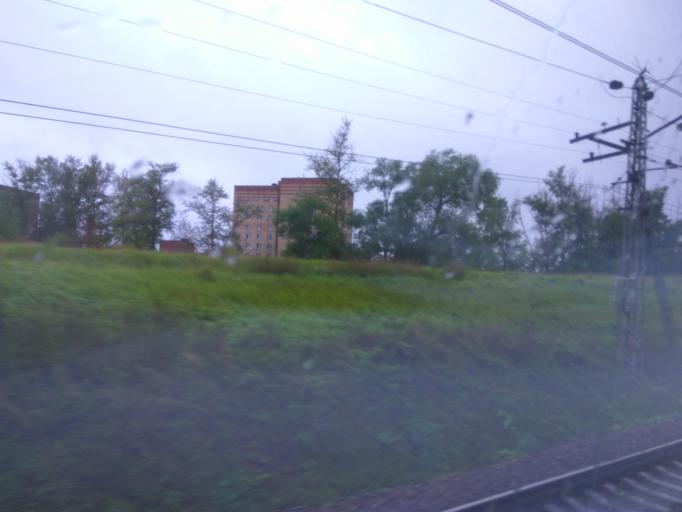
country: RU
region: Moskovskaya
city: Stupino
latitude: 54.9006
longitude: 38.0871
